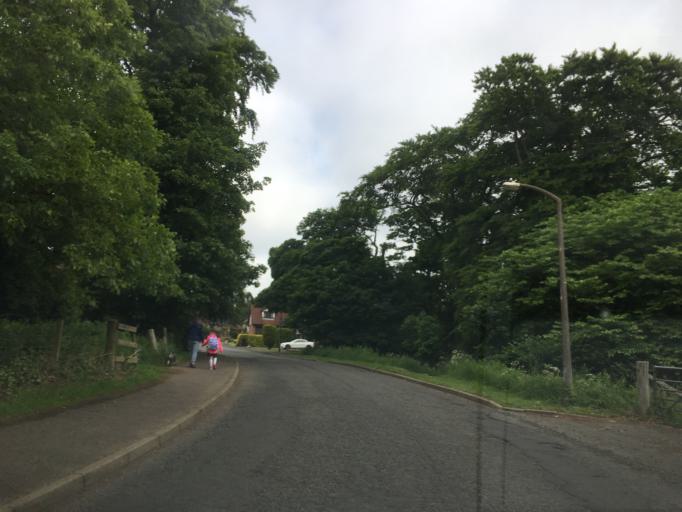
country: GB
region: Scotland
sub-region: Midlothian
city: Loanhead
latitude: 55.9031
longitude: -3.1914
